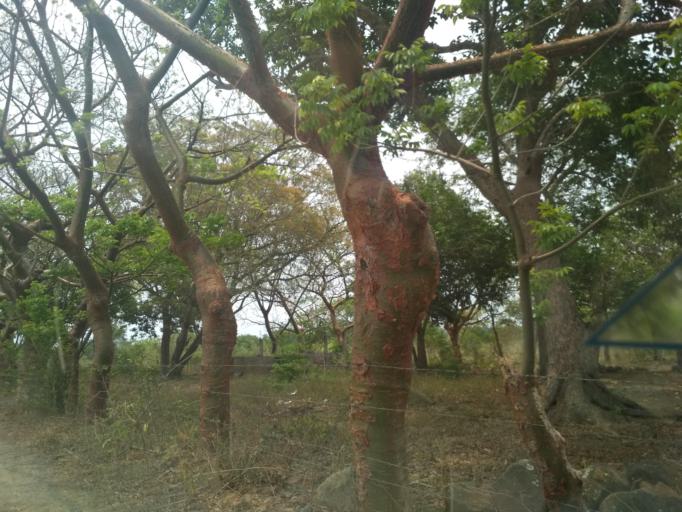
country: MX
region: Veracruz
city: Paso del Toro
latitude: 19.0517
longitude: -96.1520
